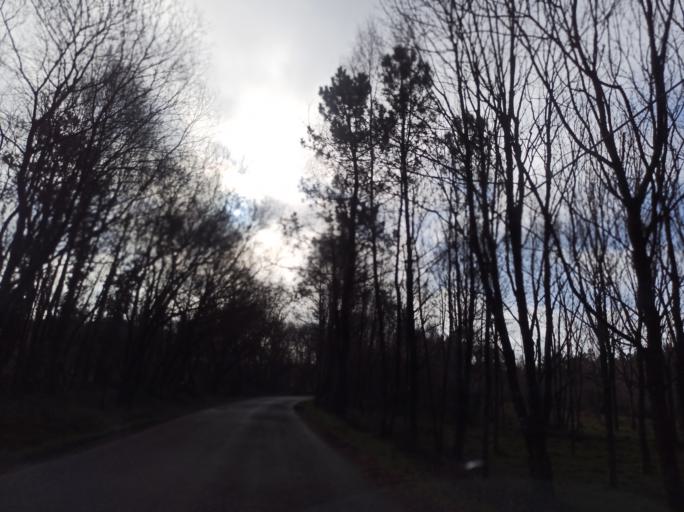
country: ES
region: Galicia
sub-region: Provincia da Coruna
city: Sobrado
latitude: 43.0949
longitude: -7.9747
